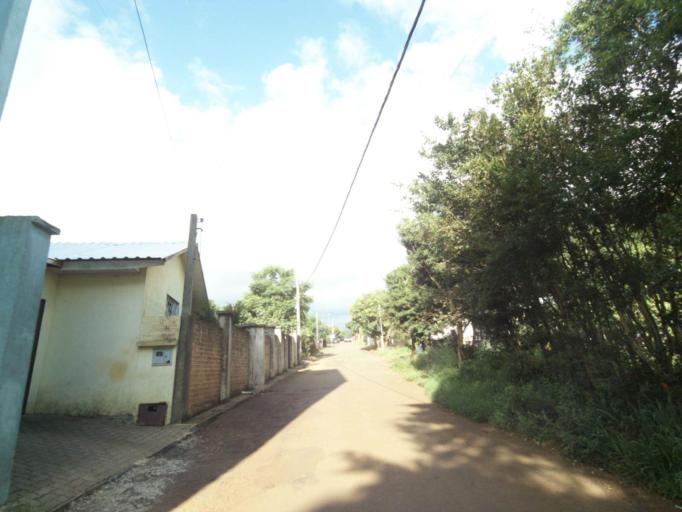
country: BR
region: Rio Grande do Sul
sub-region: Lagoa Vermelha
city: Lagoa Vermelha
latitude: -28.2035
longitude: -51.5201
